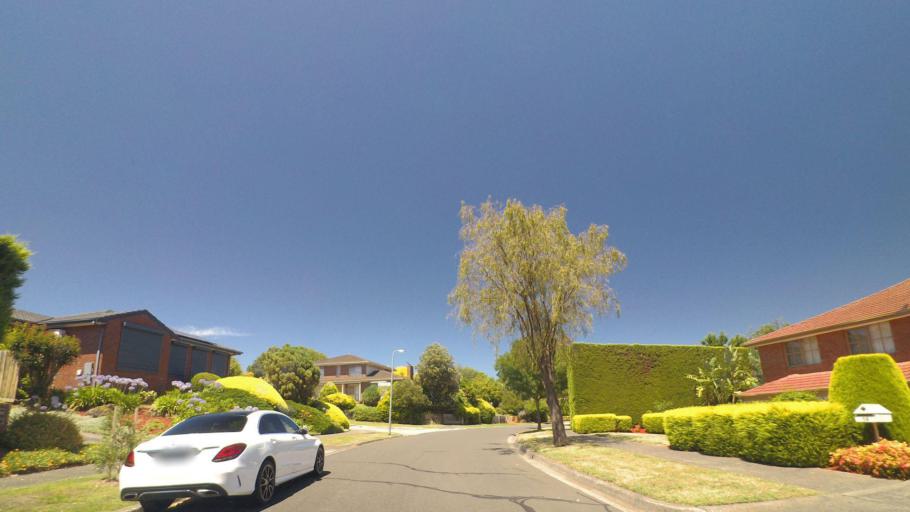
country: AU
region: Victoria
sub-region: Maroondah
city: Warranwood
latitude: -37.7874
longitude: 145.2454
